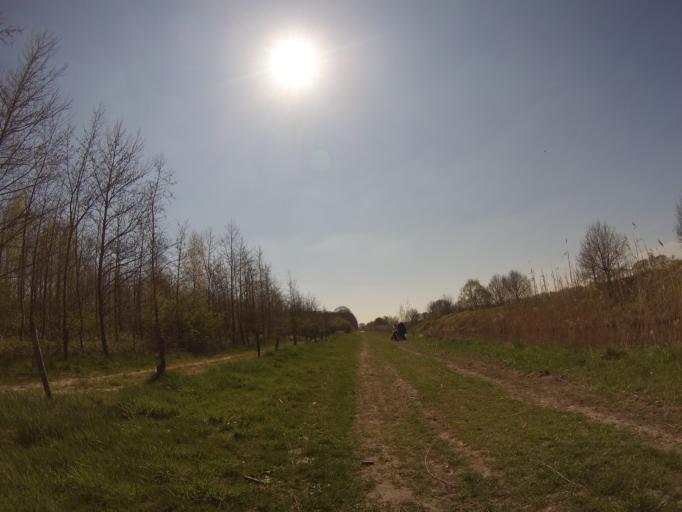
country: NL
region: Utrecht
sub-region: Gemeente Utrechtse Heuvelrug
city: Overberg
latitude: 52.0642
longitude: 5.4790
